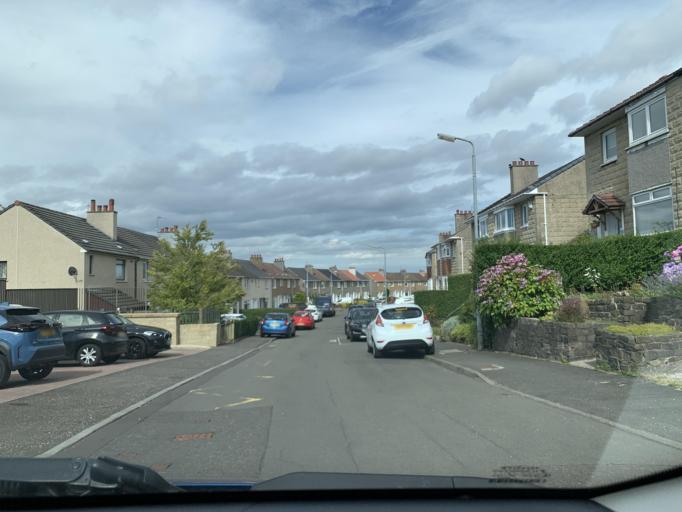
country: GB
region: Scotland
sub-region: East Renfrewshire
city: Clarkston
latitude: 55.8127
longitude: -4.2656
